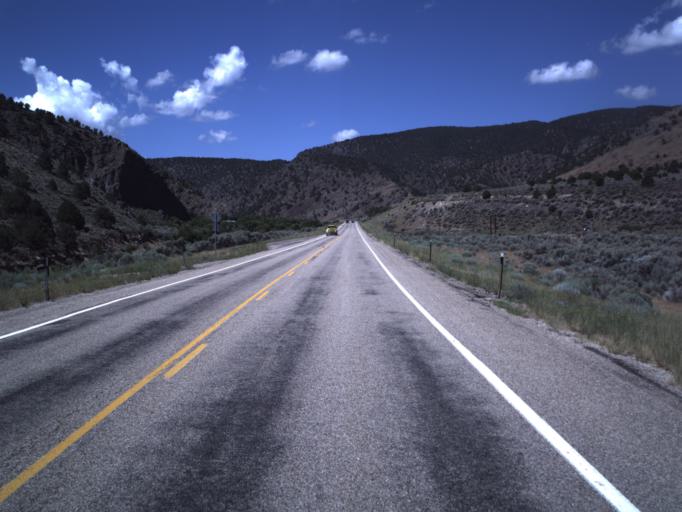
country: US
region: Utah
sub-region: Piute County
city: Junction
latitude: 38.1302
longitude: -112.3186
